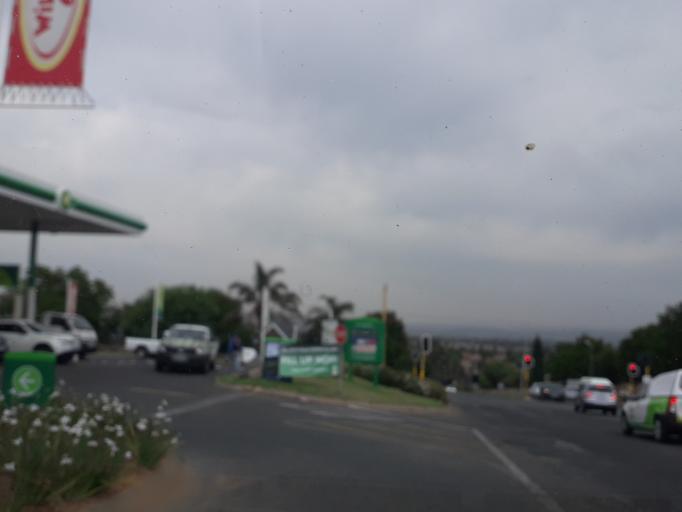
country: ZA
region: Gauteng
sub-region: City of Johannesburg Metropolitan Municipality
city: Roodepoort
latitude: -26.1043
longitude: 27.9242
